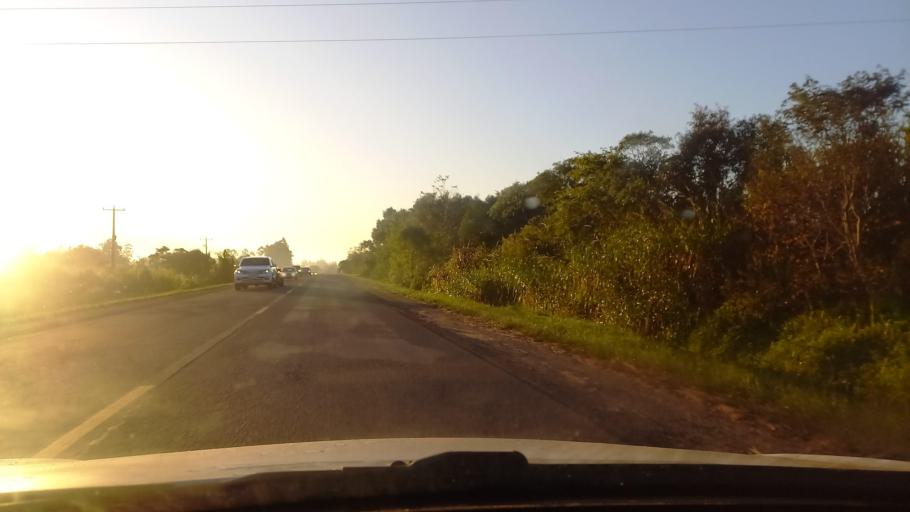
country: BR
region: Rio Grande do Sul
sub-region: Candelaria
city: Candelaria
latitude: -29.6807
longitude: -52.8304
